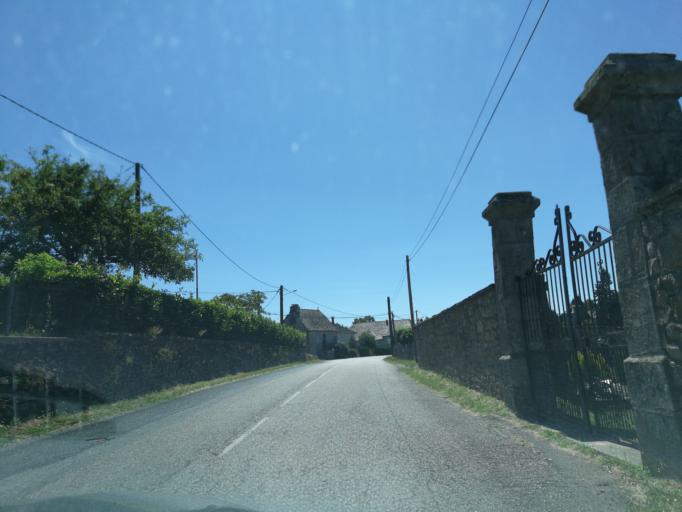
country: FR
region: Limousin
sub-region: Departement de la Correze
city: Argentat
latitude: 45.0435
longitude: 1.9527
